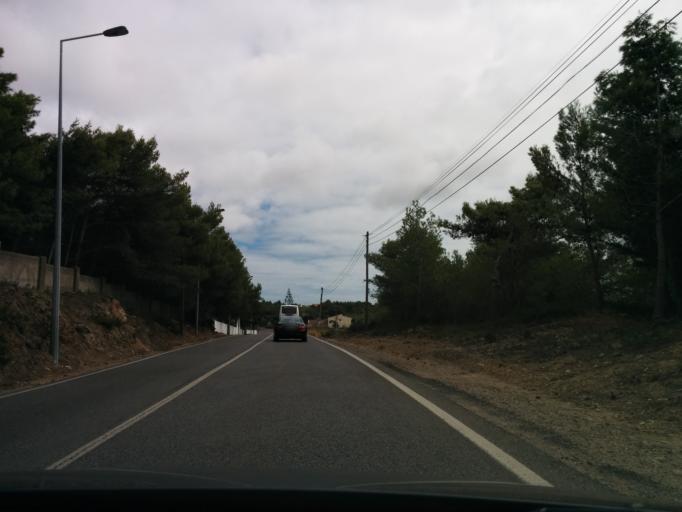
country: PT
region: Lisbon
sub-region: Cascais
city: Alcabideche
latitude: 38.7354
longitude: -9.4480
